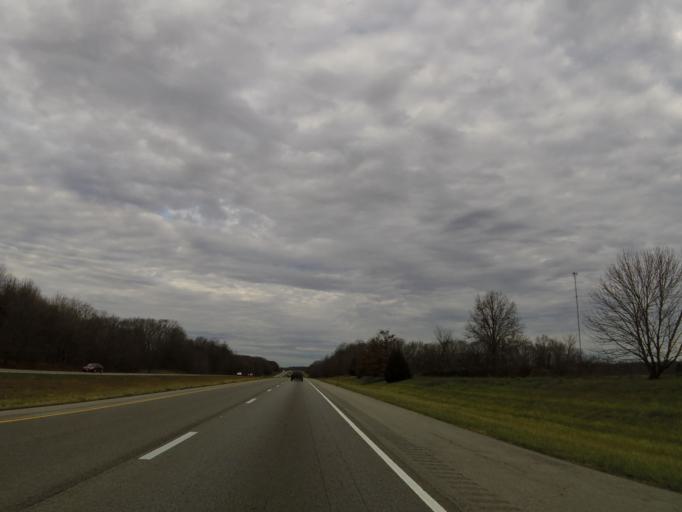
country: US
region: Illinois
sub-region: Clinton County
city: Wamac
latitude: 38.3666
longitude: -89.0884
